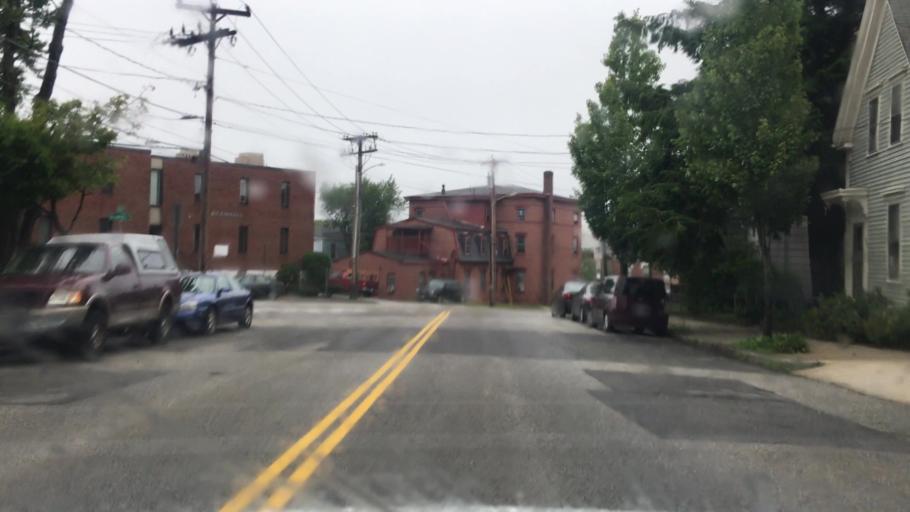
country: US
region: Maine
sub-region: Cumberland County
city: Portland
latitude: 43.6532
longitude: -70.2731
